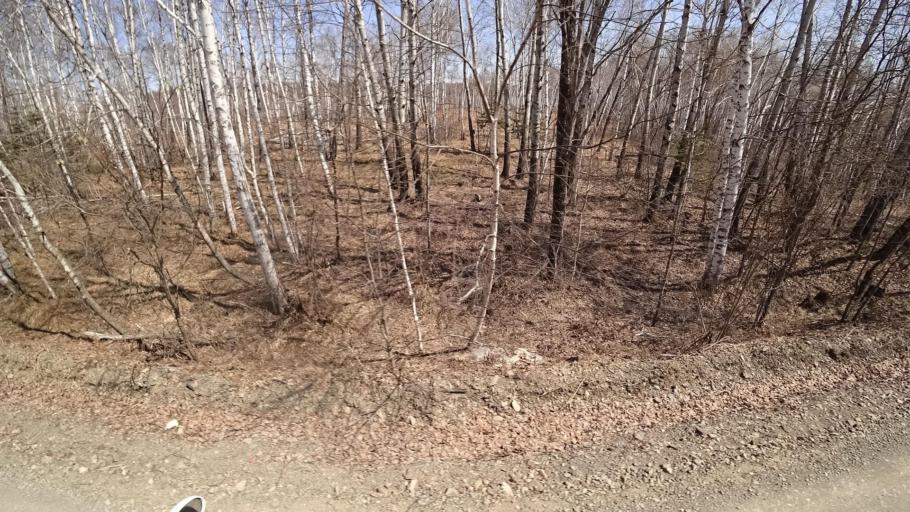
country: RU
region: Khabarovsk Krai
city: Khurba
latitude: 50.4162
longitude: 136.8383
